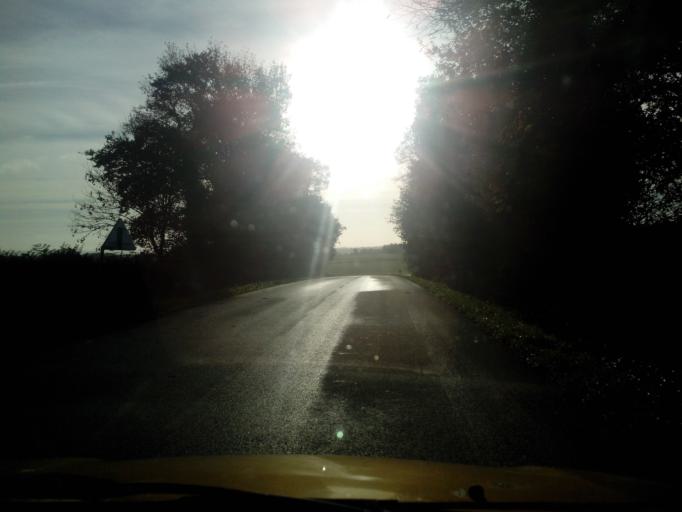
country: FR
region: Brittany
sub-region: Departement du Morbihan
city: Guilliers
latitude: 48.0656
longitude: -2.4166
